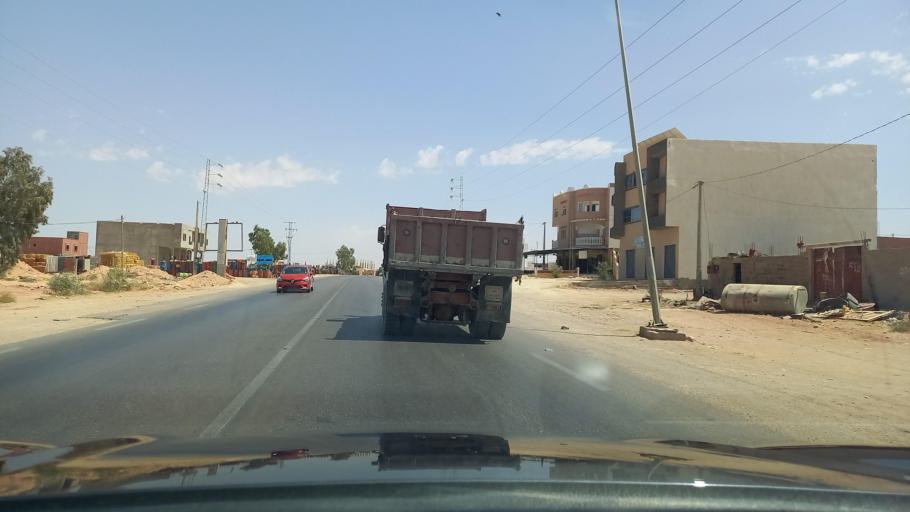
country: TN
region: Madanin
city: Medenine
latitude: 33.3673
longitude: 10.4540
